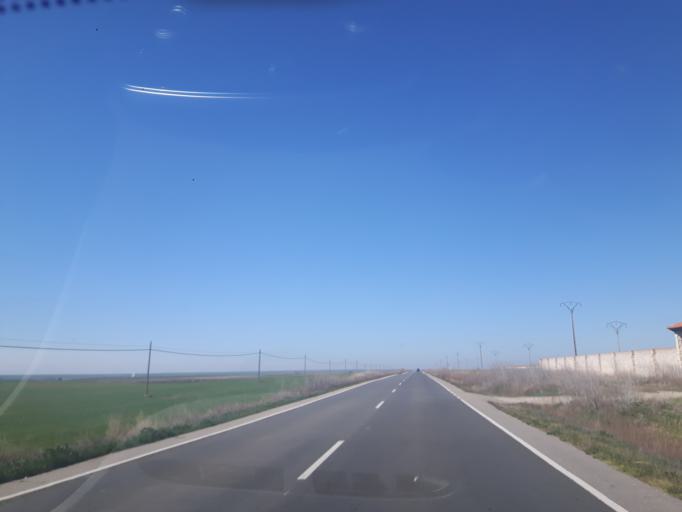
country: ES
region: Castille and Leon
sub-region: Provincia de Salamanca
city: Penaranda de Bracamonte
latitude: 40.8973
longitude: -5.2267
